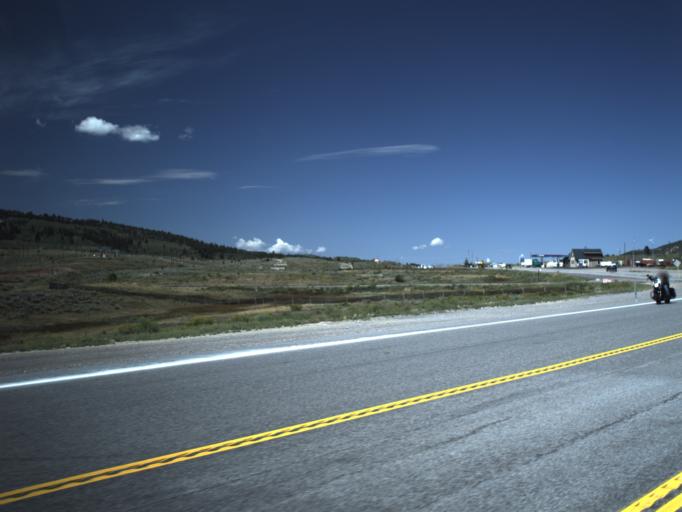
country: US
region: Utah
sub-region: Carbon County
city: Helper
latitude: 39.9278
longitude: -111.0747
